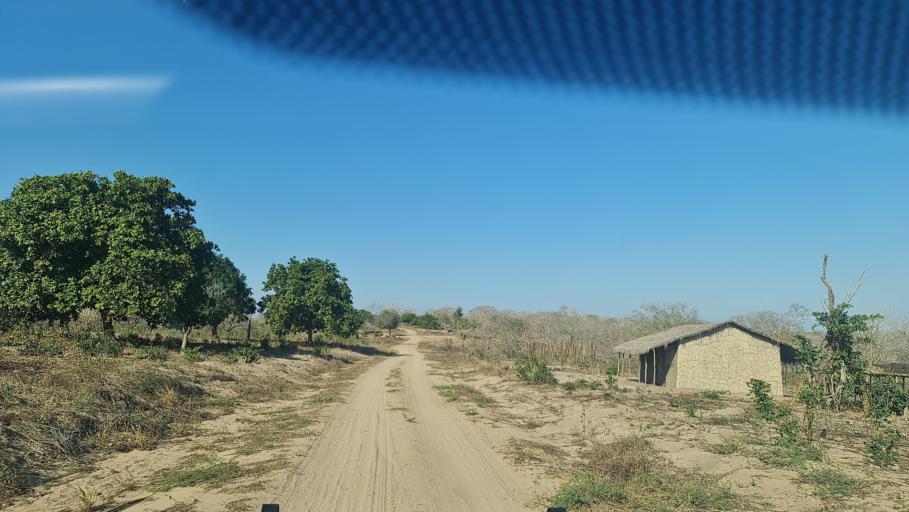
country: MZ
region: Nampula
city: Nacala
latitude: -13.9440
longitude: 40.4811
